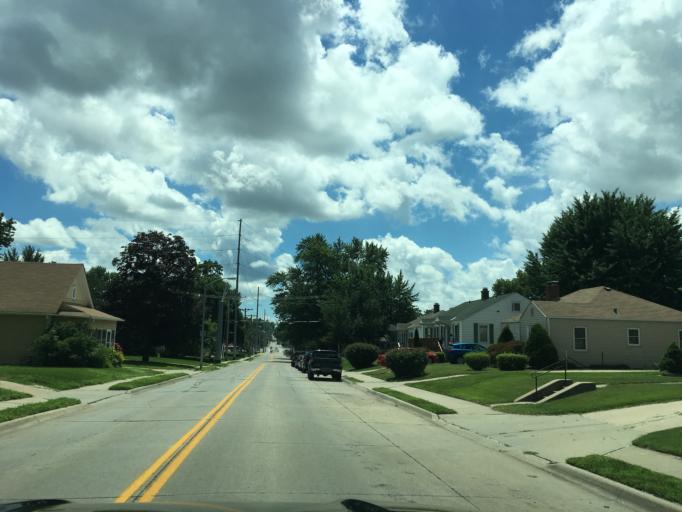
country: US
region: Nebraska
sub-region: Douglas County
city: Omaha
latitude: 41.2498
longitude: -95.9902
